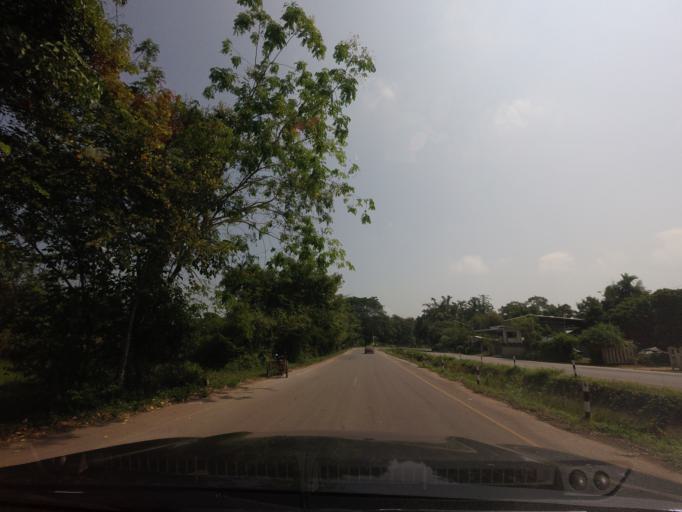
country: TH
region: Nan
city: Nan
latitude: 18.7983
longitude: 100.7590
